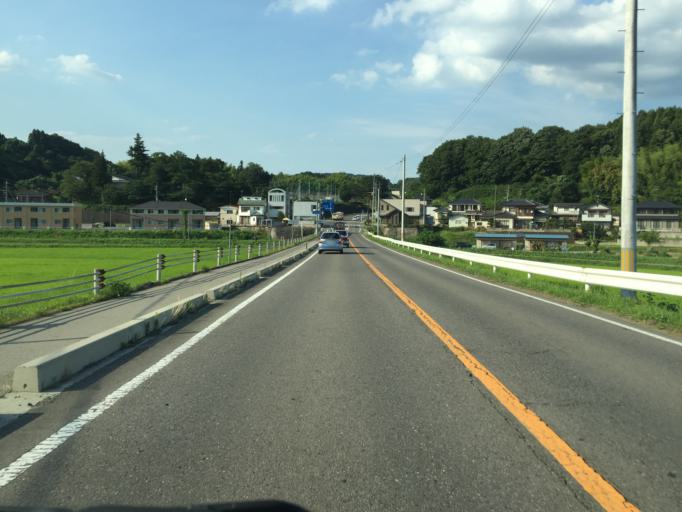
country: JP
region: Fukushima
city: Nihommatsu
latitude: 37.5851
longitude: 140.4175
